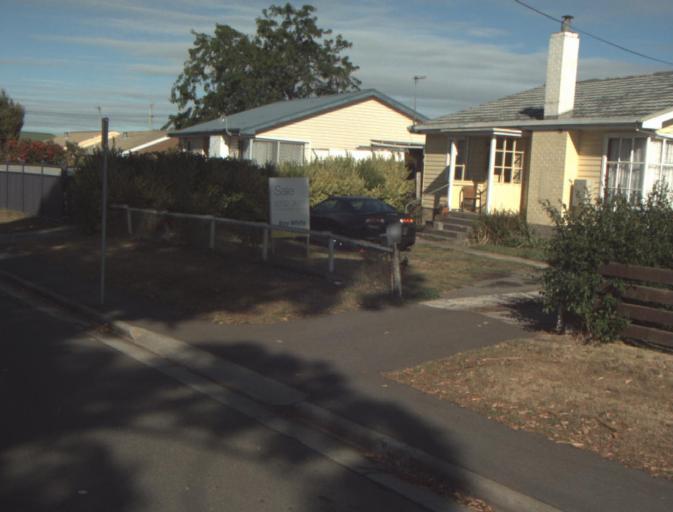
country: AU
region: Tasmania
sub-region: Launceston
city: Mayfield
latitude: -41.3865
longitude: 147.1306
